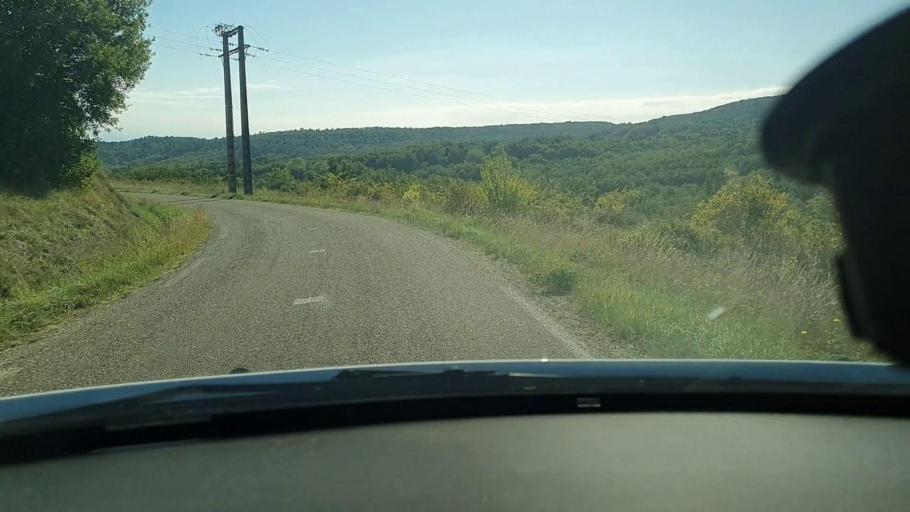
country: FR
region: Languedoc-Roussillon
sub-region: Departement du Gard
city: Saint-Julien-de-Peyrolas
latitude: 44.2641
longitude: 4.5308
